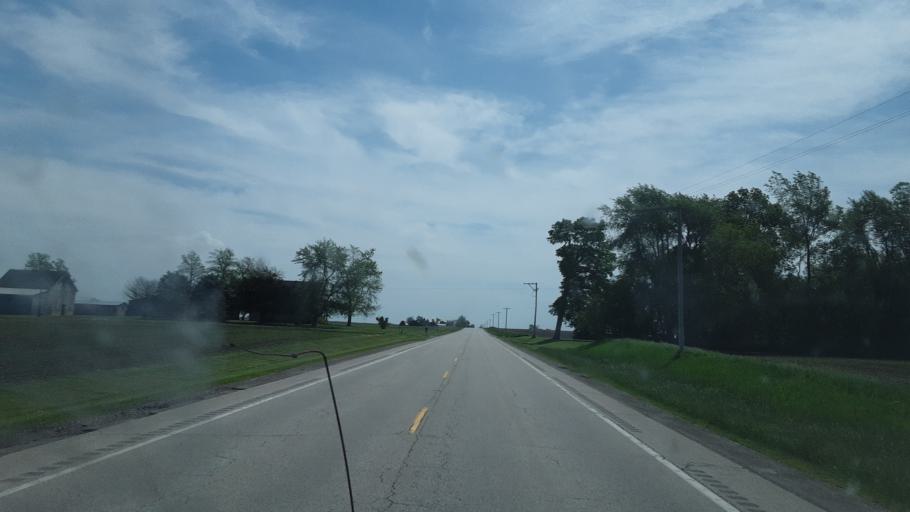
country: US
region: Illinois
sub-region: McLean County
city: Heyworth
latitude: 40.3124
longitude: -88.9150
